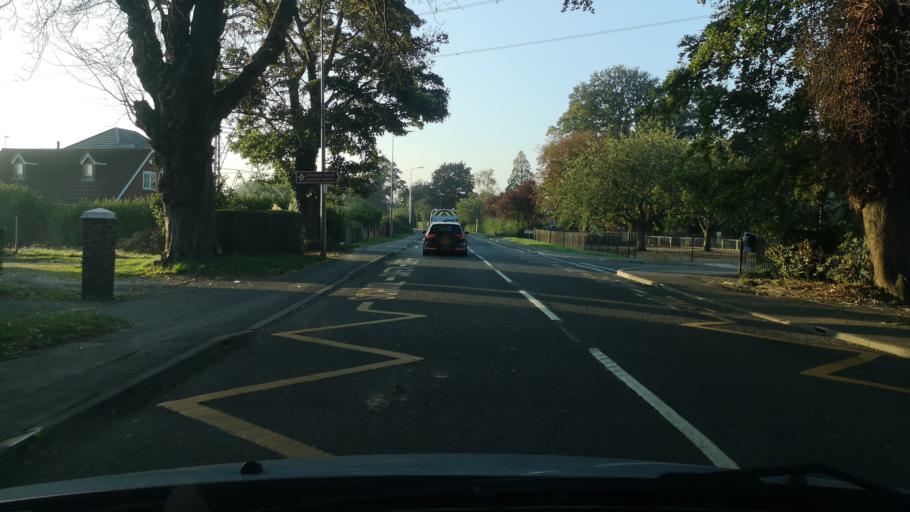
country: GB
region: England
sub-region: North Lincolnshire
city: Crowle
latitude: 53.6005
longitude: -0.8274
